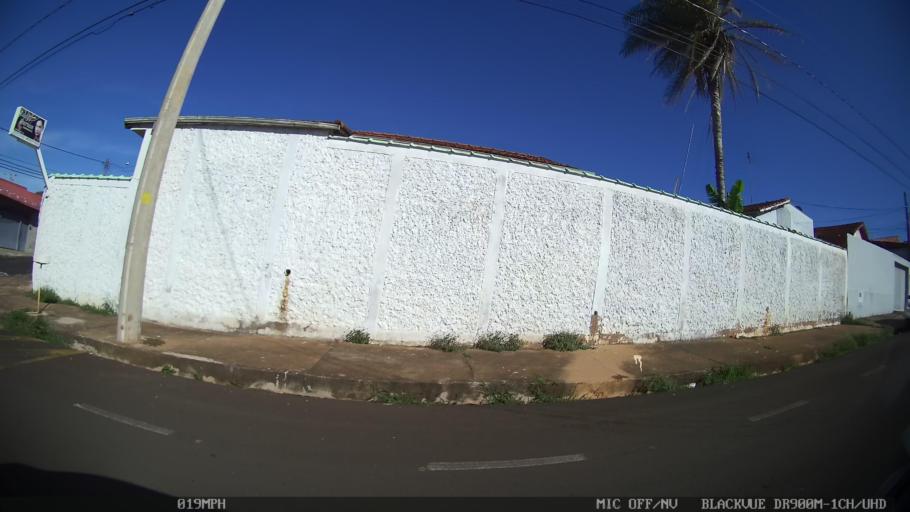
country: BR
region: Sao Paulo
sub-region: Franca
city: Franca
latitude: -20.5483
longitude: -47.4110
